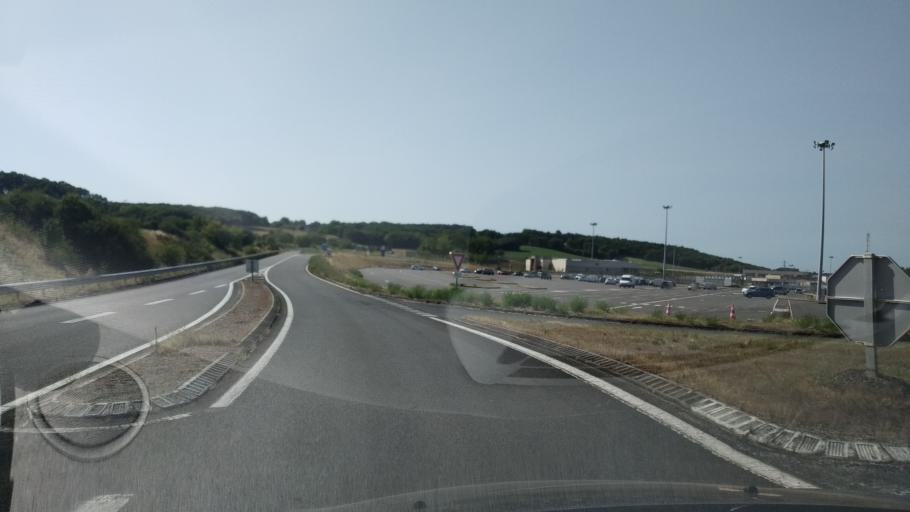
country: FR
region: Poitou-Charentes
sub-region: Departement de la Vienne
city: Lussac-les-Chateaux
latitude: 46.4476
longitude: 0.6536
